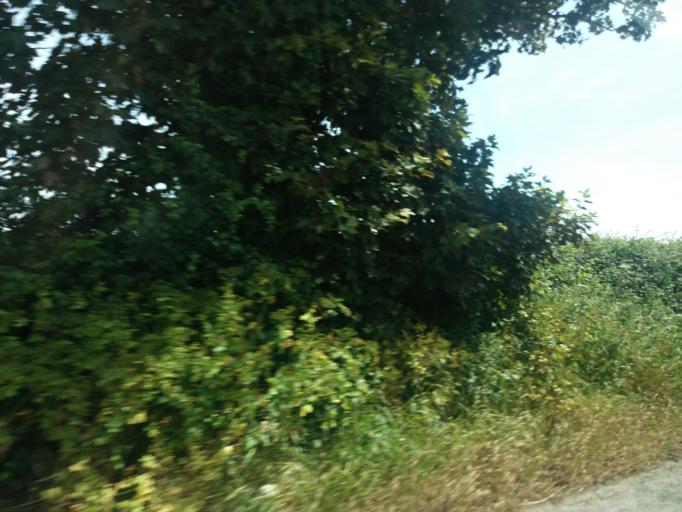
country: IE
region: Leinster
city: Lusk
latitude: 53.5432
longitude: -6.2035
